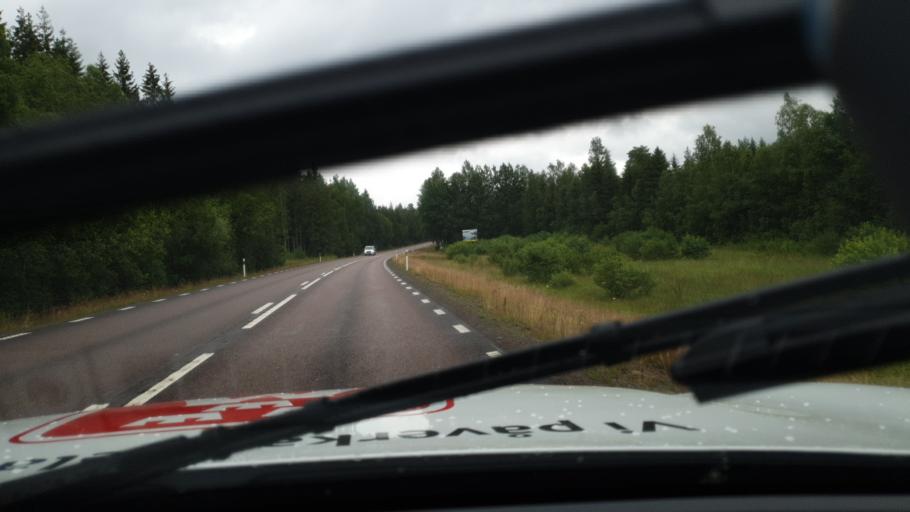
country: SE
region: Vaermland
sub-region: Storfors Kommun
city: Storfors
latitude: 59.5169
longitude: 14.2695
